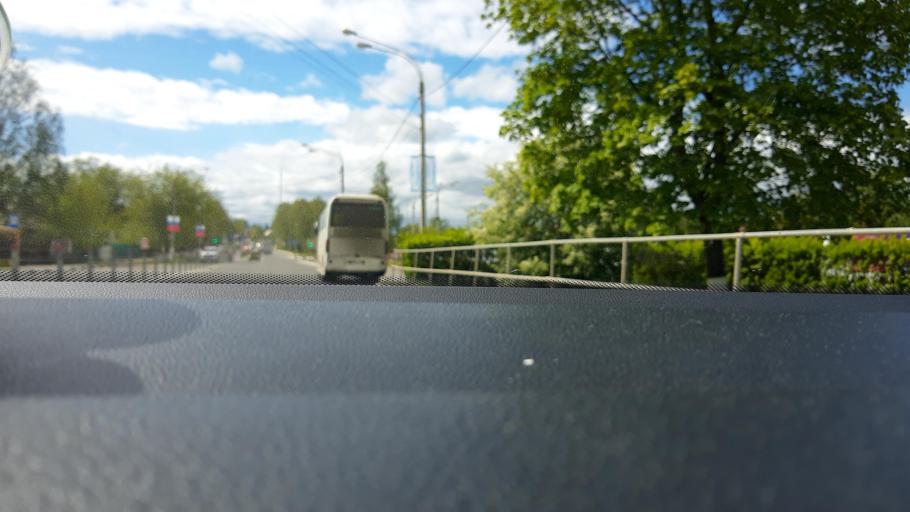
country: RU
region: Moskovskaya
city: Dmitrov
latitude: 56.3368
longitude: 37.5130
